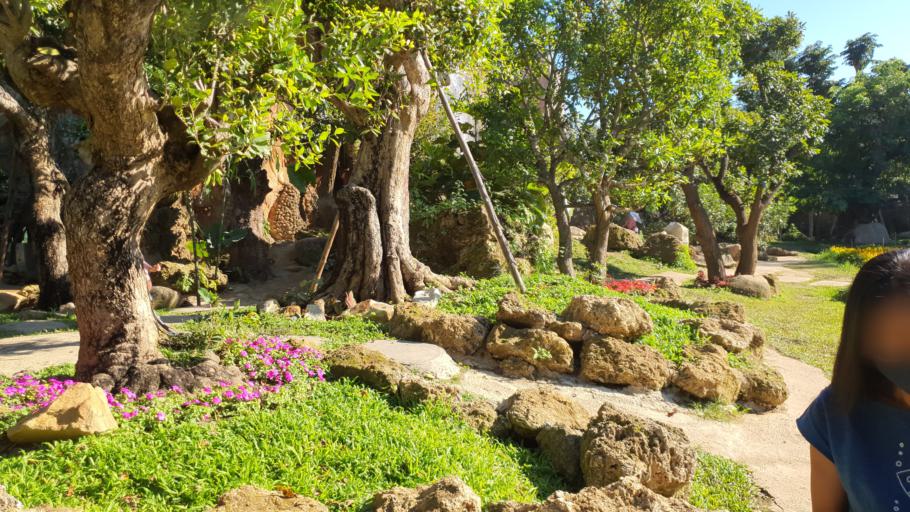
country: TH
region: Chiang Mai
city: Mae Taeng
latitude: 19.1235
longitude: 98.9429
